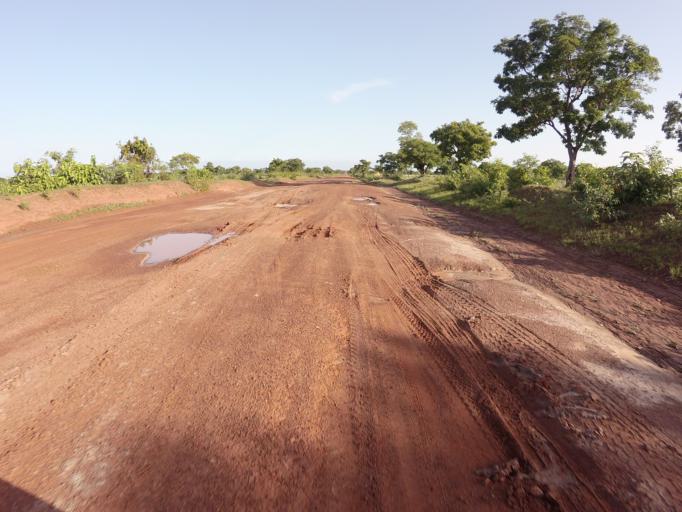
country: TG
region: Savanes
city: Sansanne-Mango
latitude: 10.3776
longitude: -0.0944
